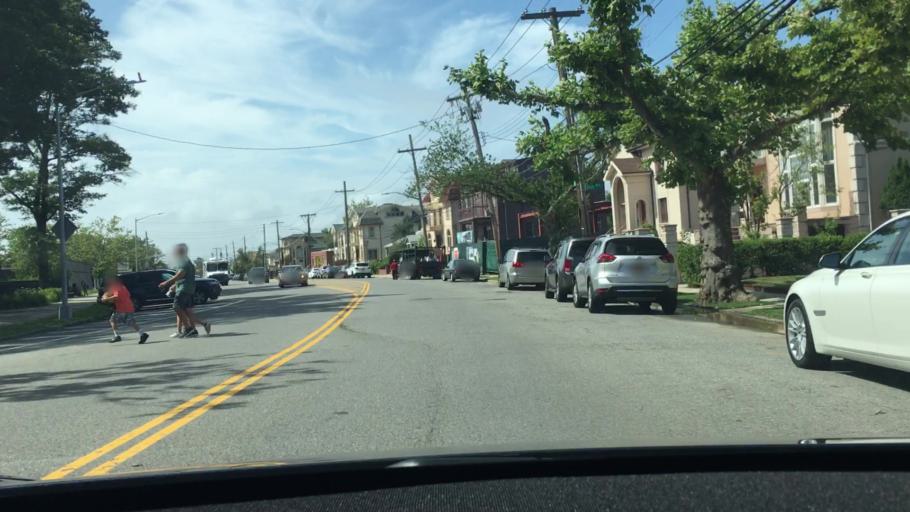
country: US
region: New York
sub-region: Kings County
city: Brooklyn
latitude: 40.6124
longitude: -73.9106
